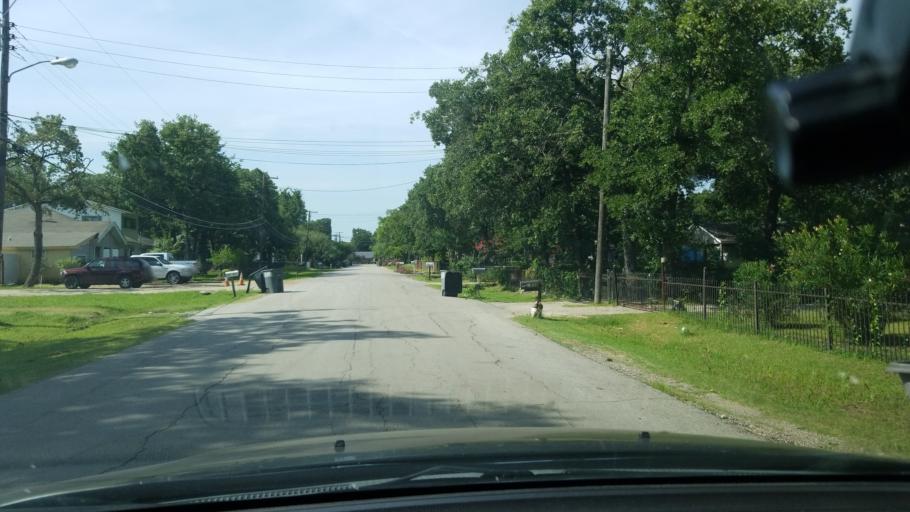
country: US
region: Texas
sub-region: Dallas County
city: Balch Springs
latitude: 32.7326
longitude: -96.6367
